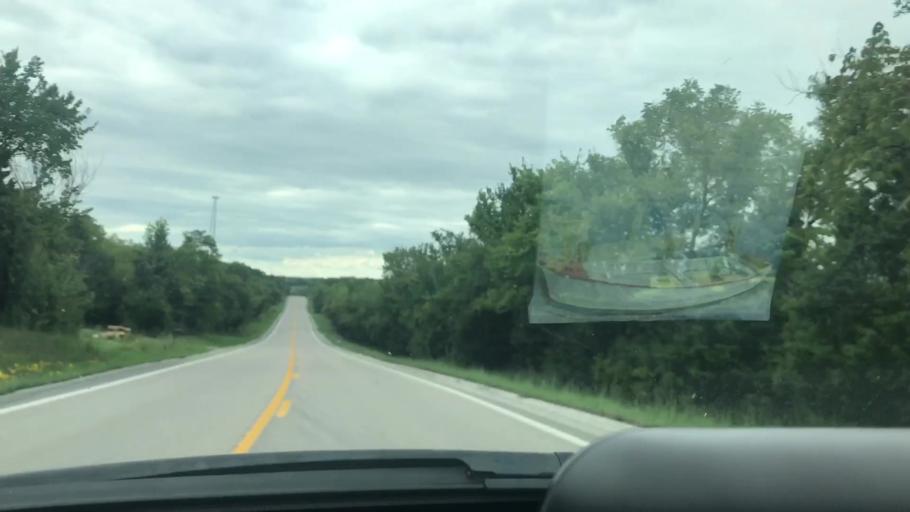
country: US
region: Missouri
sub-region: Benton County
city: Warsaw
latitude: 38.1704
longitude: -93.3114
